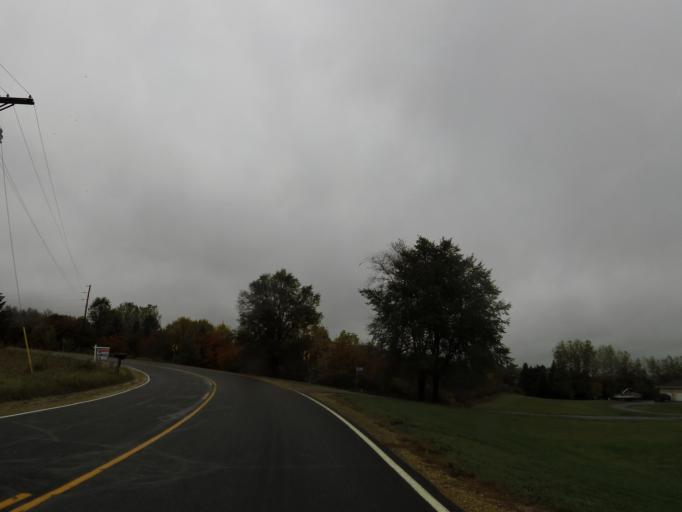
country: US
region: Minnesota
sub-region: Scott County
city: Prior Lake
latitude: 44.6909
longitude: -93.4190
